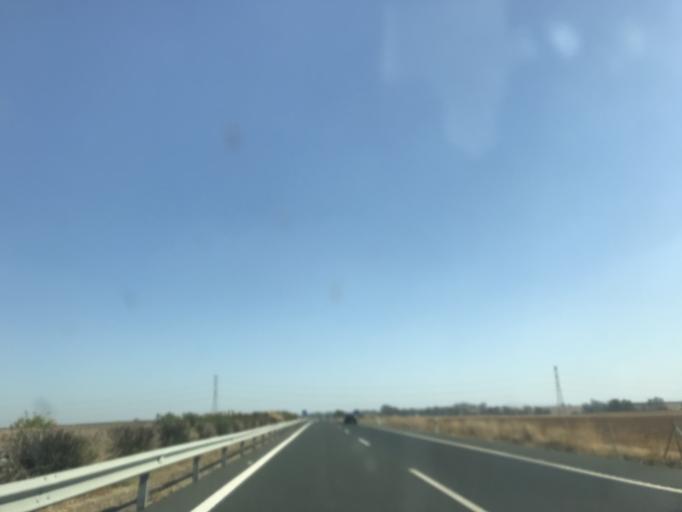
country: ES
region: Andalusia
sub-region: Provincia de Sevilla
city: Mairena del Alcor
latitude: 37.3169
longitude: -5.7611
